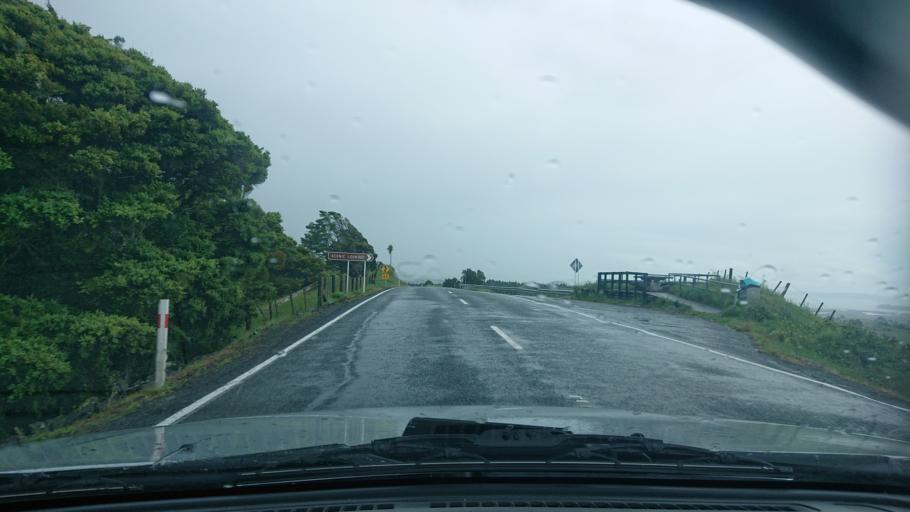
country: NZ
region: Auckland
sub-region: Auckland
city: Wellsford
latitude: -36.3514
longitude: 174.4719
